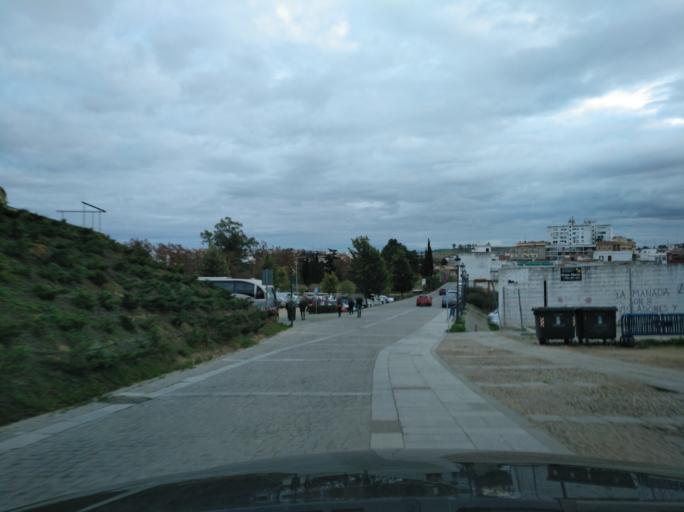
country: ES
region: Extremadura
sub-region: Provincia de Badajoz
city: Badajoz
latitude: 38.8808
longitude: -6.9660
